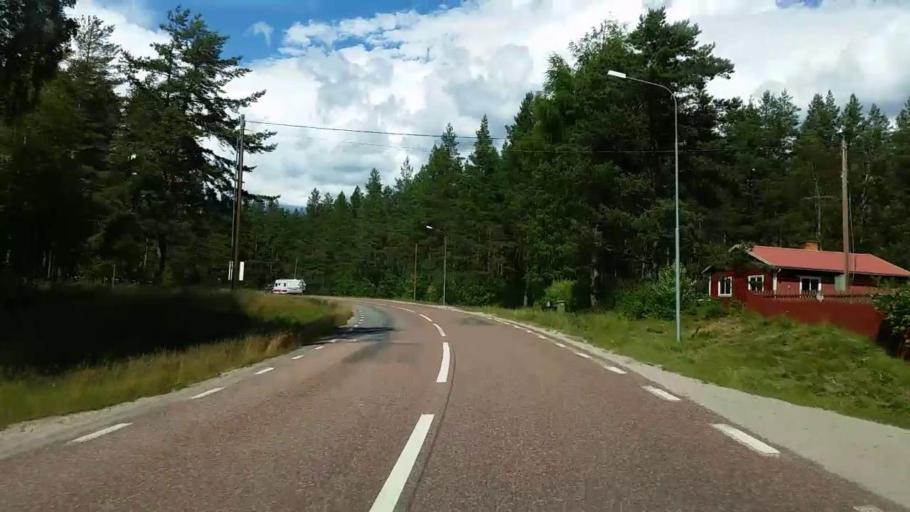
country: SE
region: Gaevleborg
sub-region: Ovanakers Kommun
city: Edsbyn
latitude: 61.3054
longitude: 15.5104
